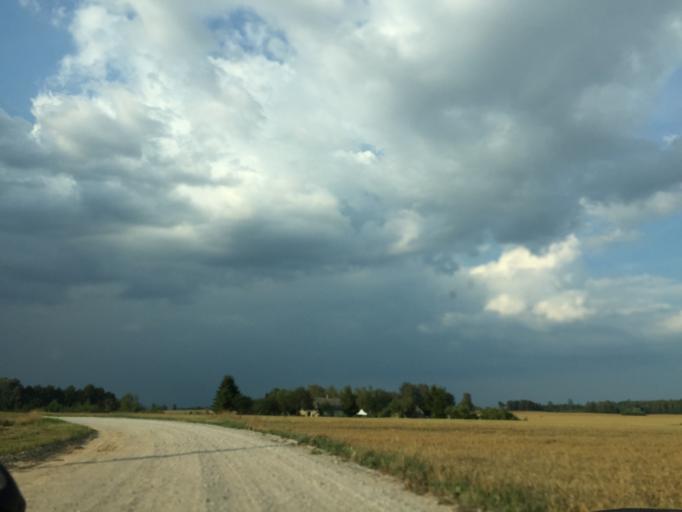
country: LV
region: Dobeles Rajons
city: Dobele
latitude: 56.5871
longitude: 23.3066
